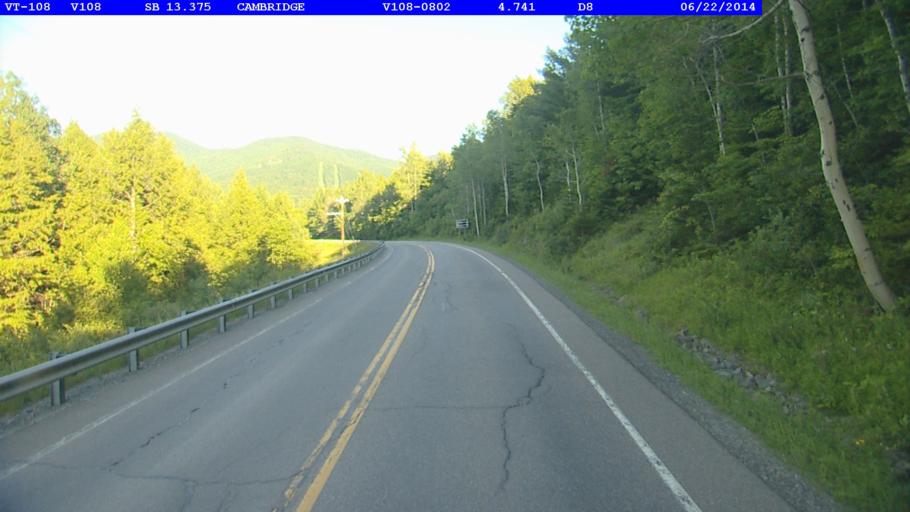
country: US
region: Vermont
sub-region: Lamoille County
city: Johnson
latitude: 44.5947
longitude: -72.8014
